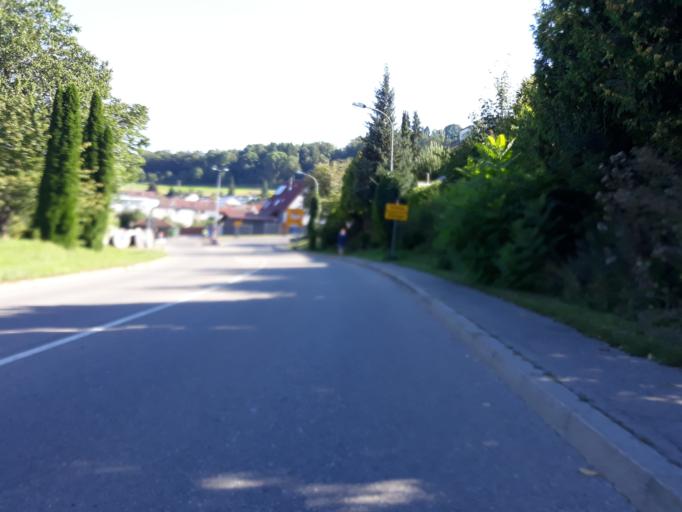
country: DE
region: Baden-Wuerttemberg
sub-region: Regierungsbezirk Stuttgart
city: Aidlingen
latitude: 48.6804
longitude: 8.9045
